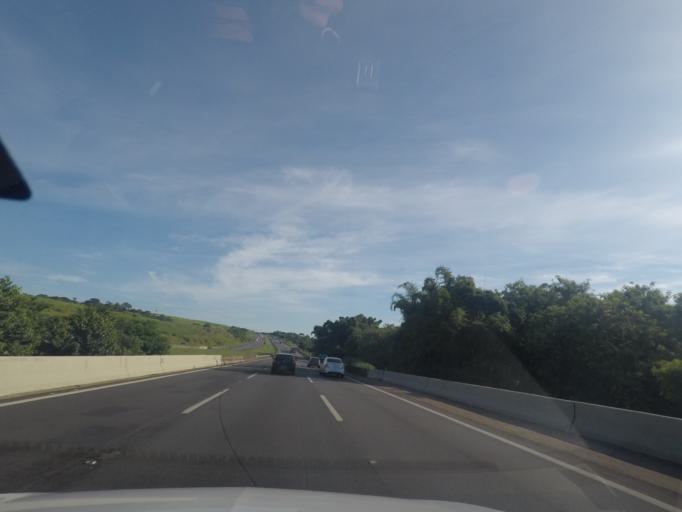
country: BR
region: Sao Paulo
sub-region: Americana
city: Americana
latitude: -22.6869
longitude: -47.3106
